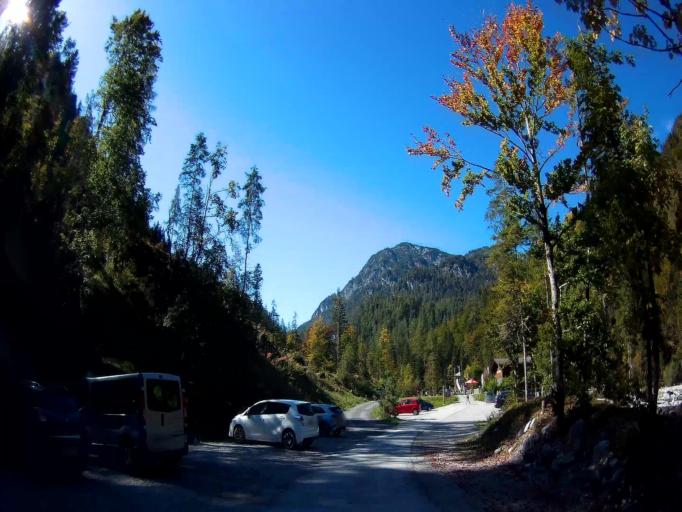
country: AT
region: Salzburg
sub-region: Politischer Bezirk Zell am See
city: Sankt Martin bei Lofer
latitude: 47.5204
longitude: 12.7065
